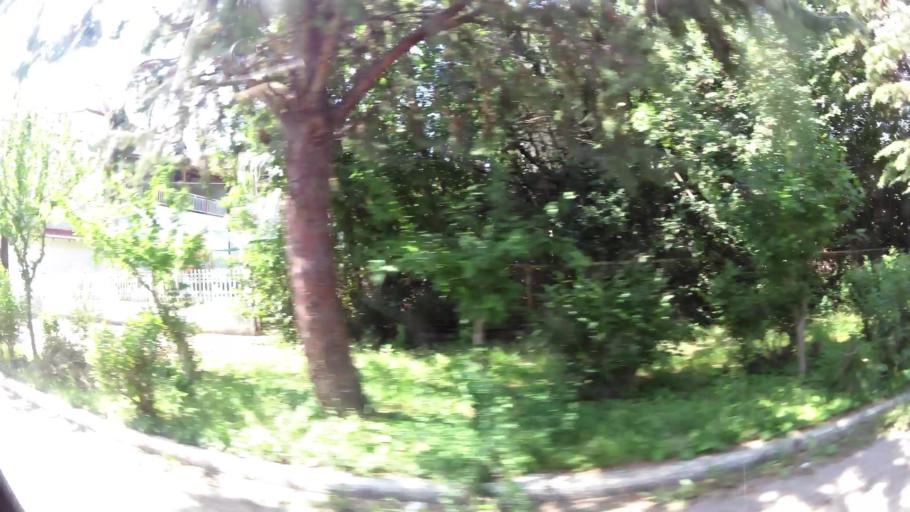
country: GR
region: West Macedonia
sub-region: Nomos Kozanis
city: Koila
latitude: 40.3362
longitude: 21.7898
